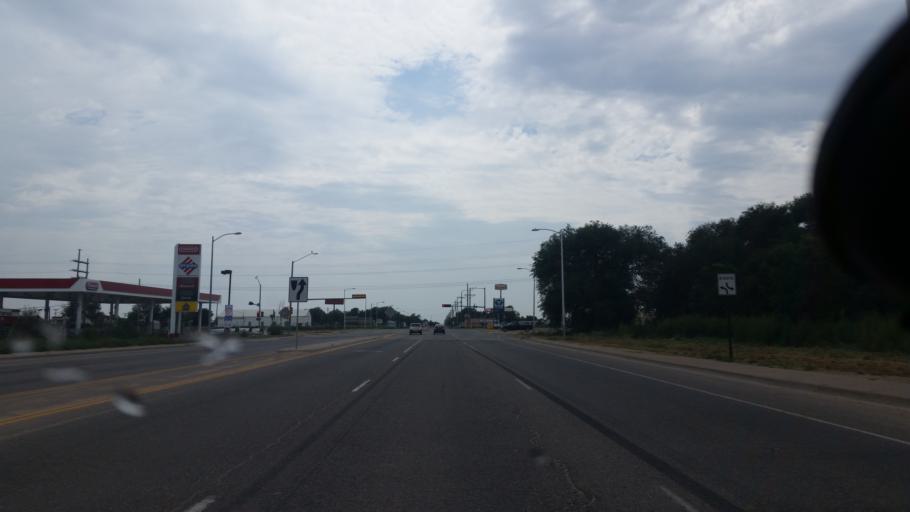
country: US
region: New Mexico
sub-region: Curry County
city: Clovis
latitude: 34.3915
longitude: -103.1965
